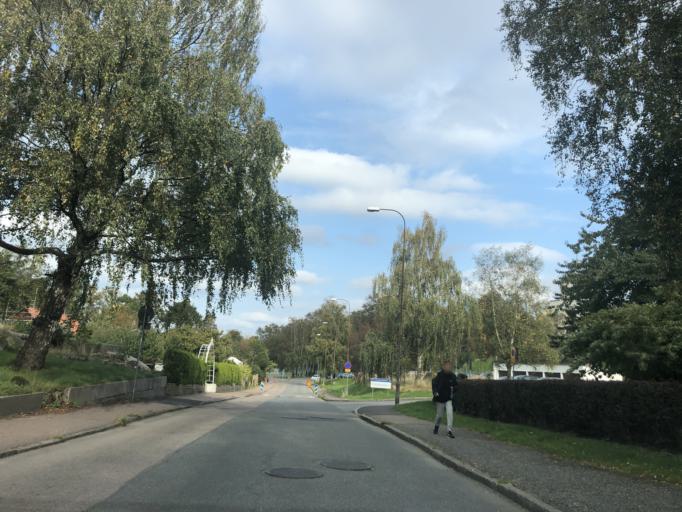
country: SE
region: Vaestra Goetaland
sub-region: Goteborg
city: Majorna
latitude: 57.6525
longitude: 11.8917
